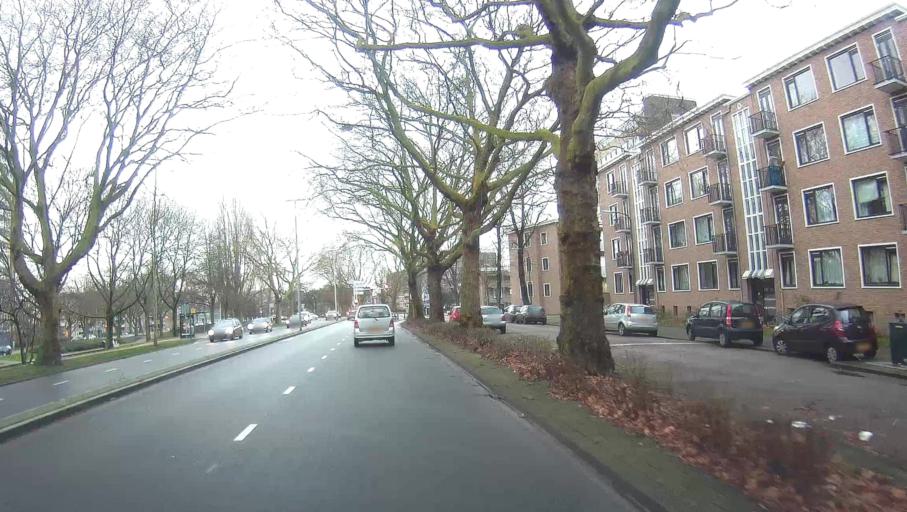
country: NL
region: South Holland
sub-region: Gemeente Den Haag
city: The Hague
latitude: 52.0521
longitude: 4.2980
